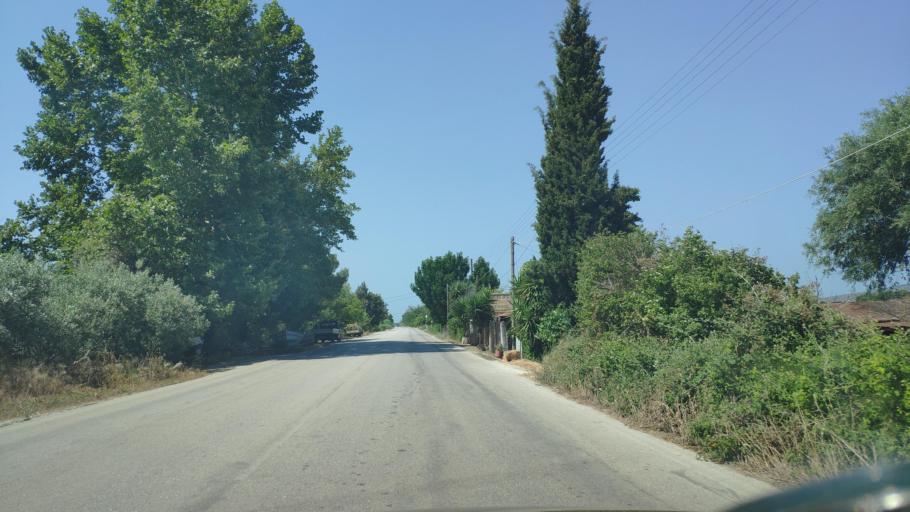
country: GR
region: Epirus
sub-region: Nomos Artas
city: Aneza
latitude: 39.1128
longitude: 20.9263
